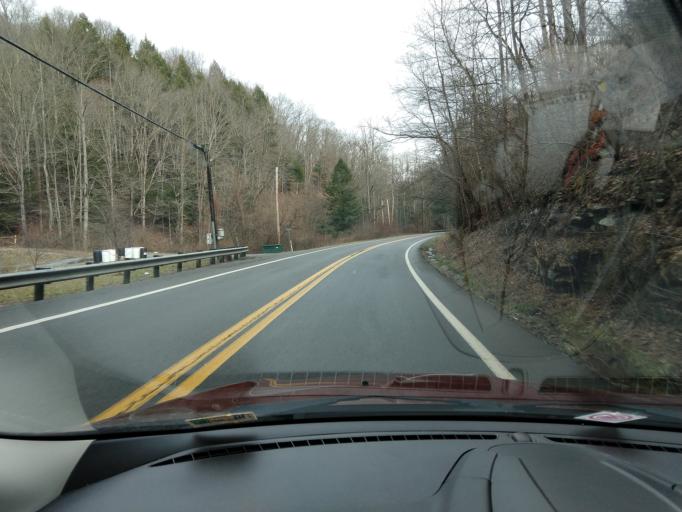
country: US
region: West Virginia
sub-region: Wyoming County
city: Pineville
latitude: 37.5501
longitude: -81.5759
